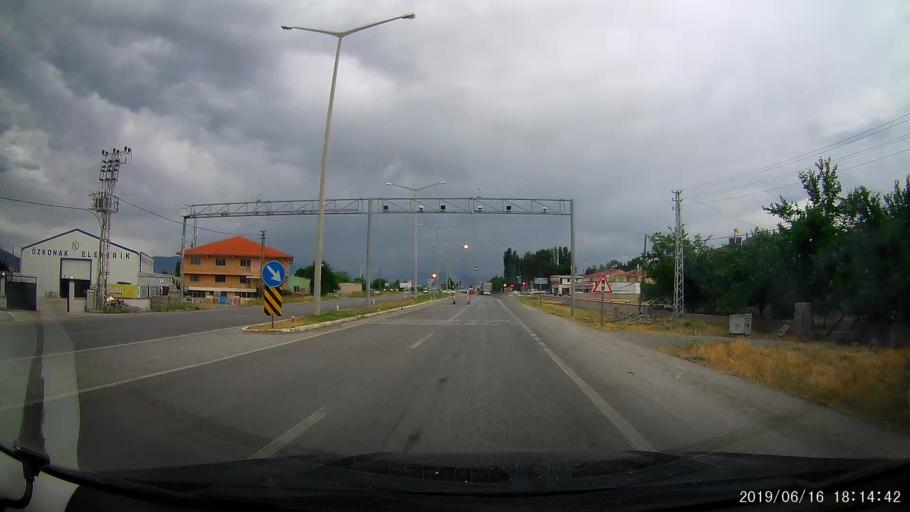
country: TR
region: Erzincan
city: Erzincan
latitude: 39.7258
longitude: 39.5543
